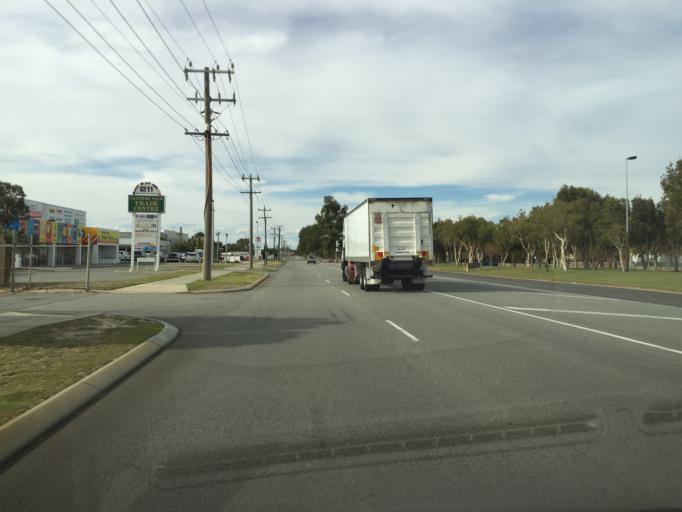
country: AU
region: Western Australia
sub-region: Canning
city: Willetton
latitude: -32.0662
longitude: 115.8998
